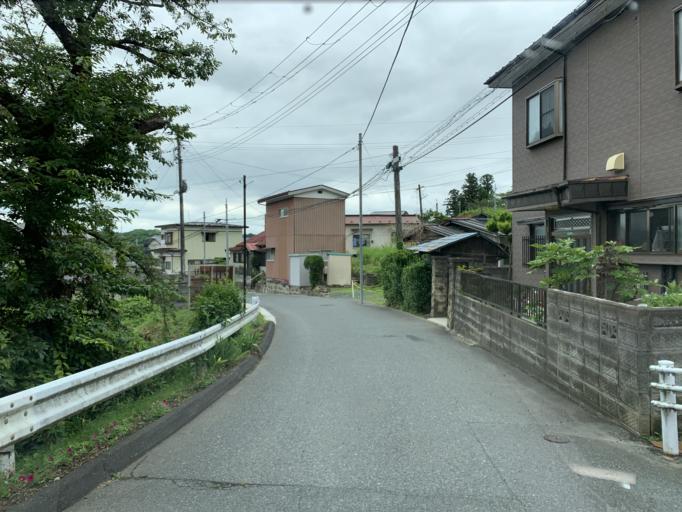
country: JP
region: Iwate
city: Ichinoseki
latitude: 38.9223
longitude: 141.1302
